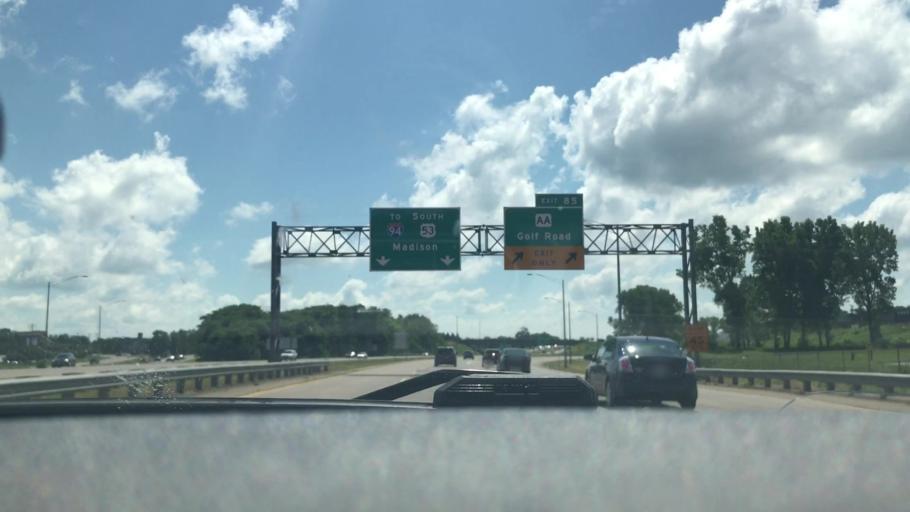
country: US
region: Wisconsin
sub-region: Eau Claire County
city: Altoona
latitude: 44.7804
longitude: -91.4405
